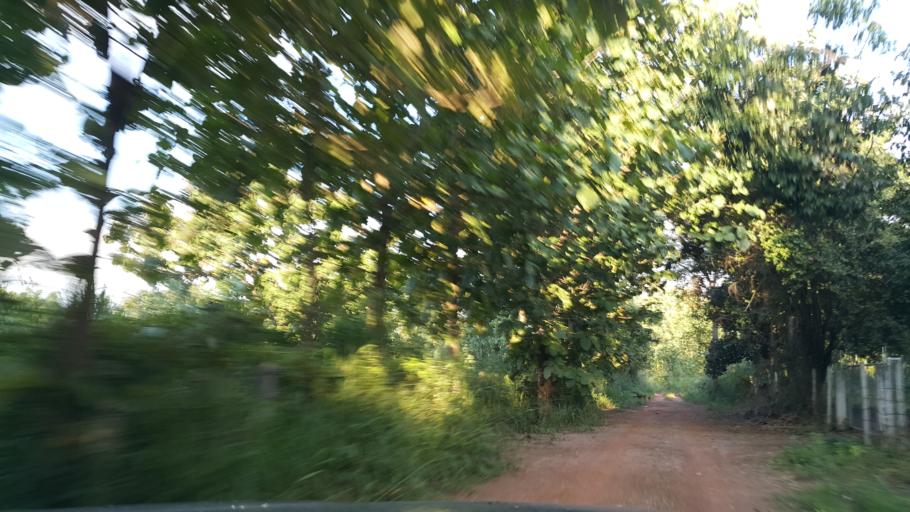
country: TH
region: Chiang Mai
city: Mae On
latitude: 18.7441
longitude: 99.2460
